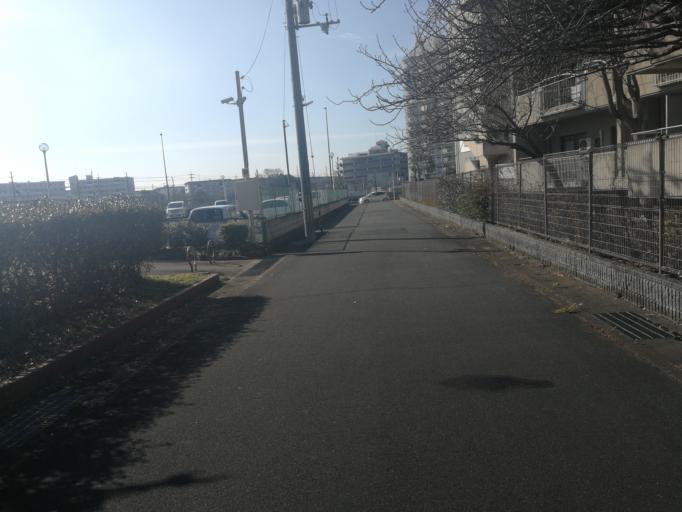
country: JP
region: Kyoto
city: Uji
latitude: 34.9184
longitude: 135.7804
